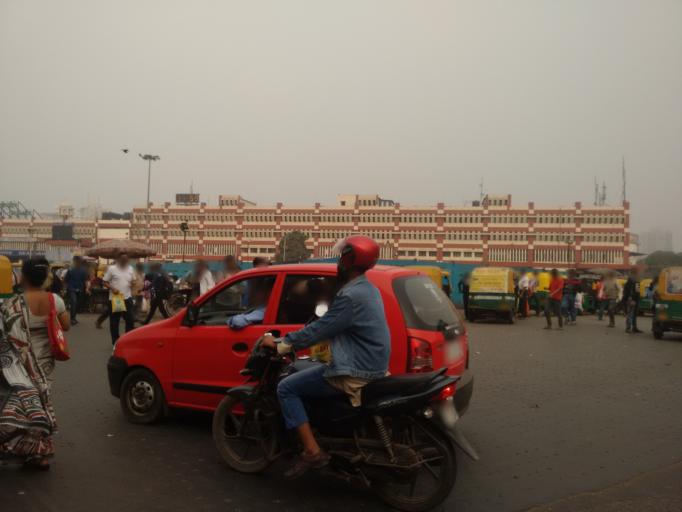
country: IN
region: West Bengal
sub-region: Kolkata
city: Kolkata
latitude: 22.5663
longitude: 88.3700
